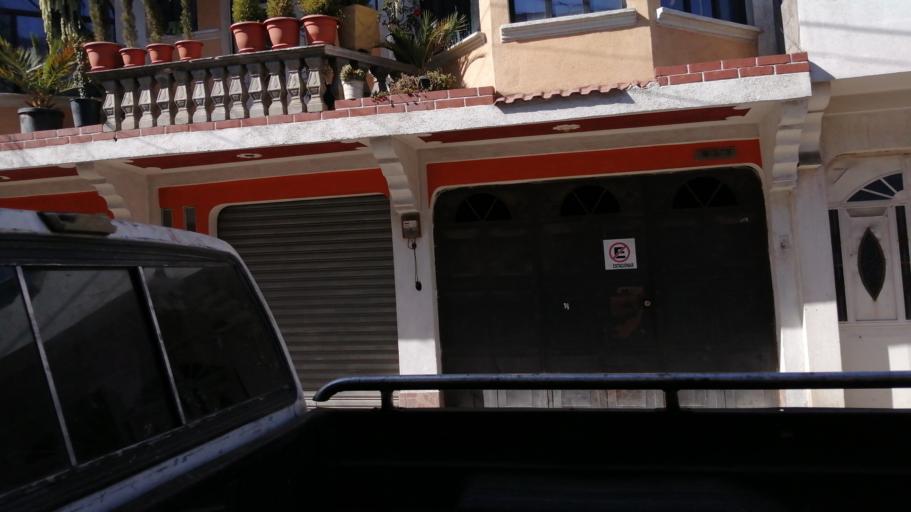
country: GT
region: Quetzaltenango
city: Ostuncalco
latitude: 14.8700
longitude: -91.6240
